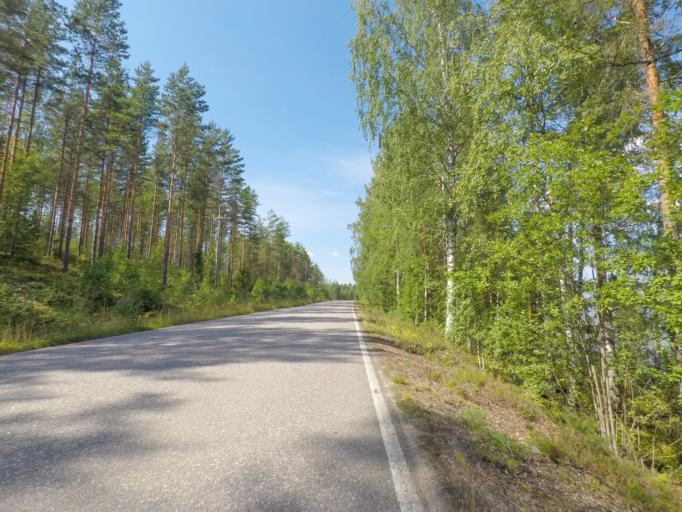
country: FI
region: Southern Savonia
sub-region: Mikkeli
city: Puumala
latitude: 61.4638
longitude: 28.1716
